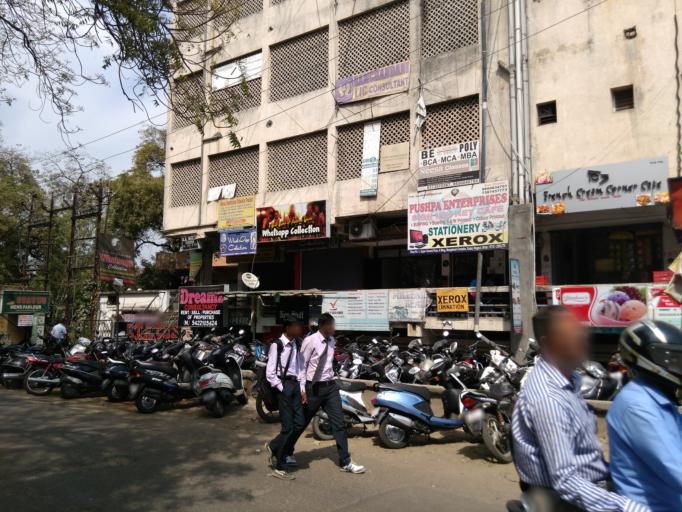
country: IN
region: Maharashtra
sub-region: Nagpur Division
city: Nagpur
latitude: 21.1650
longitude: 79.0813
